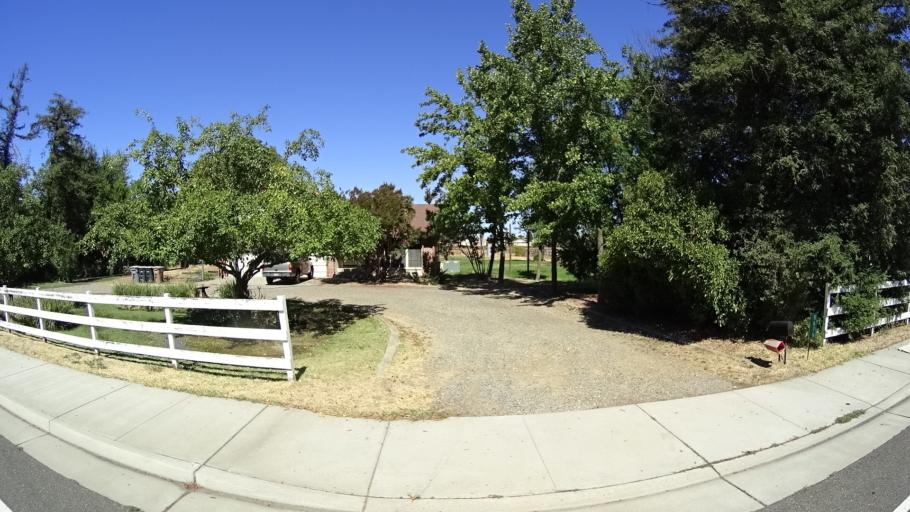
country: US
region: California
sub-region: Sacramento County
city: Elk Grove
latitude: 38.4381
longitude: -121.3818
